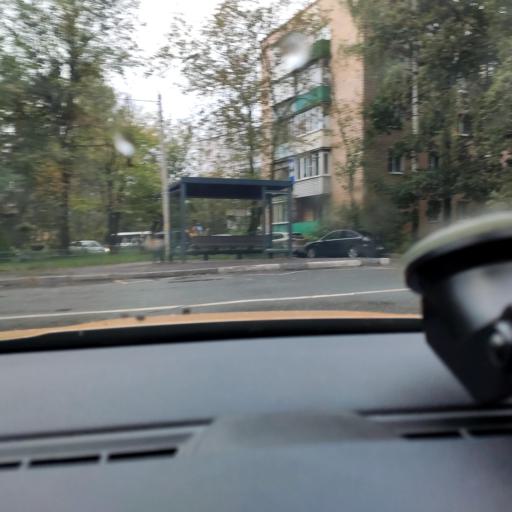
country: RU
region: Moskovskaya
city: Druzhba
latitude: 55.8852
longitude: 37.7546
